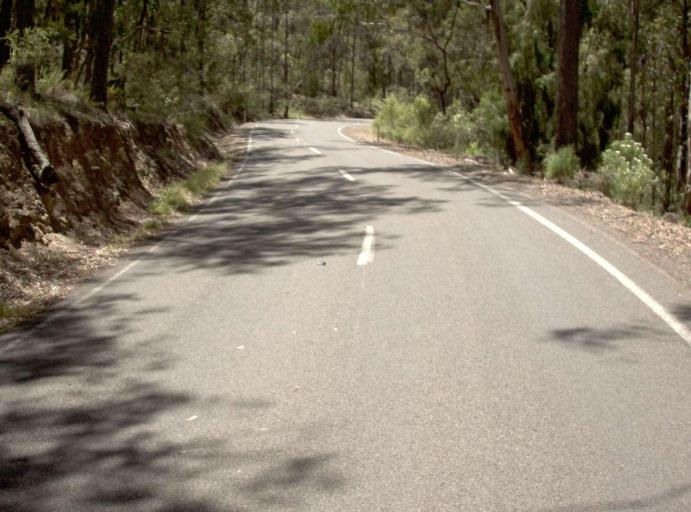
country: AU
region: Victoria
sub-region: East Gippsland
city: Lakes Entrance
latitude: -37.6039
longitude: 147.8840
